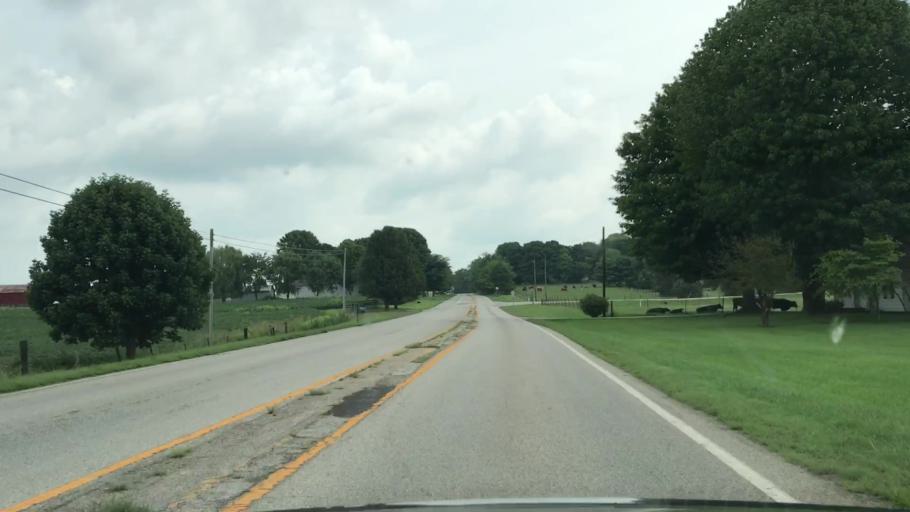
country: US
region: Kentucky
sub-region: Barren County
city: Cave City
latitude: 37.1115
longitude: -85.9896
